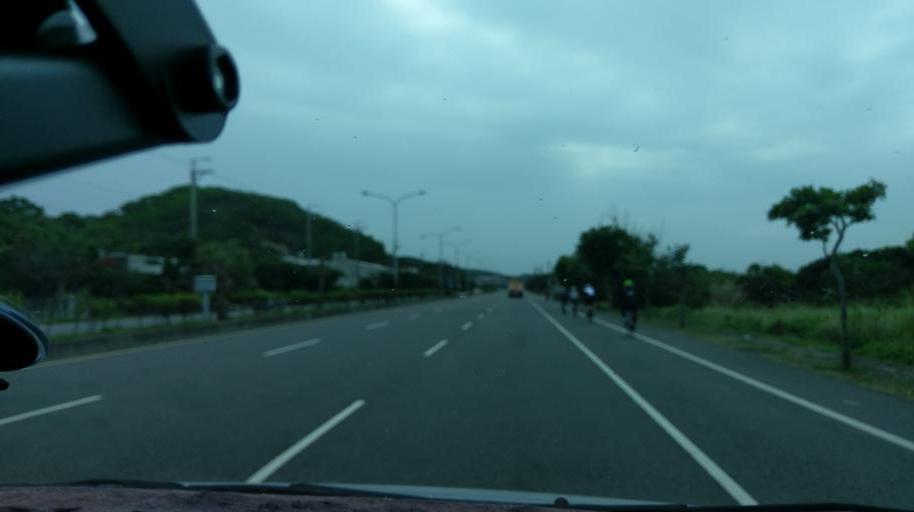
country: TW
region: Taiwan
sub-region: Miaoli
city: Miaoli
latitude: 24.5220
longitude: 120.6921
